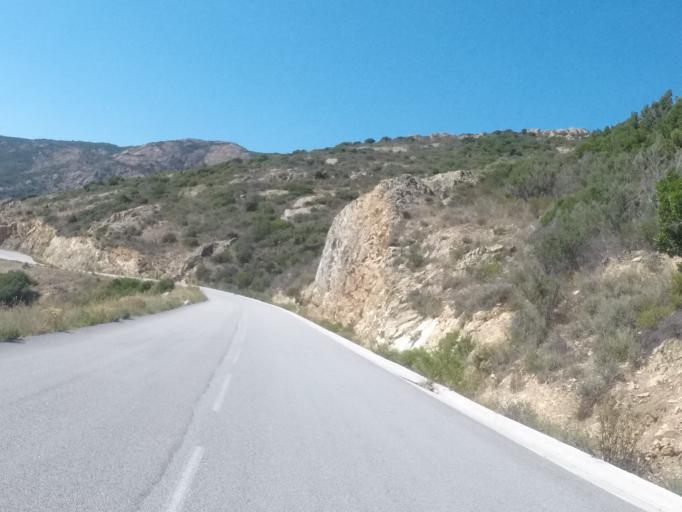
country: FR
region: Corsica
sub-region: Departement de la Haute-Corse
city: Calvi
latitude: 42.4763
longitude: 8.7549
